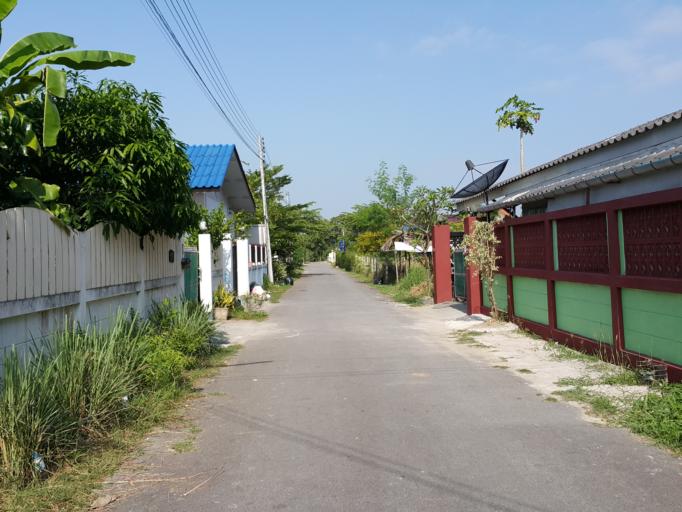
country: TH
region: Chiang Mai
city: San Kamphaeng
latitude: 18.7805
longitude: 99.0975
